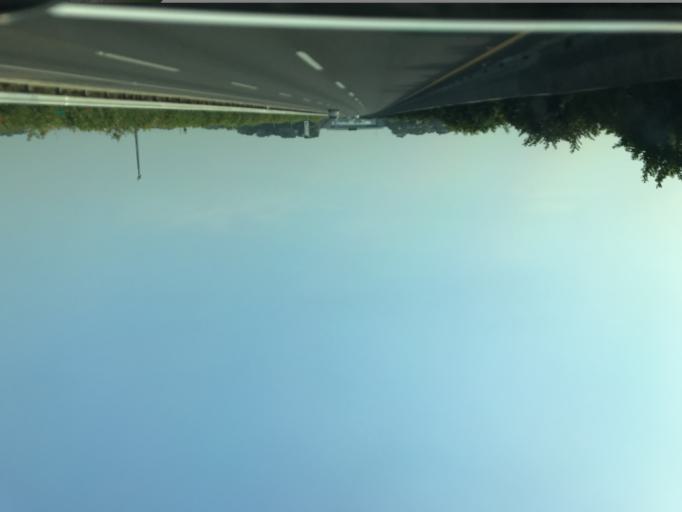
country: TW
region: Taiwan
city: Xinying
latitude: 23.3658
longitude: 120.3461
